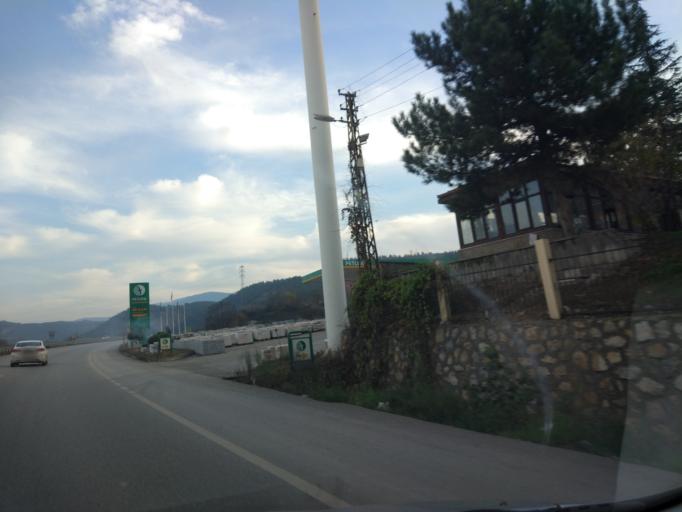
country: TR
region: Karabuk
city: Karabuk
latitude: 41.1561
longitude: 32.6508
